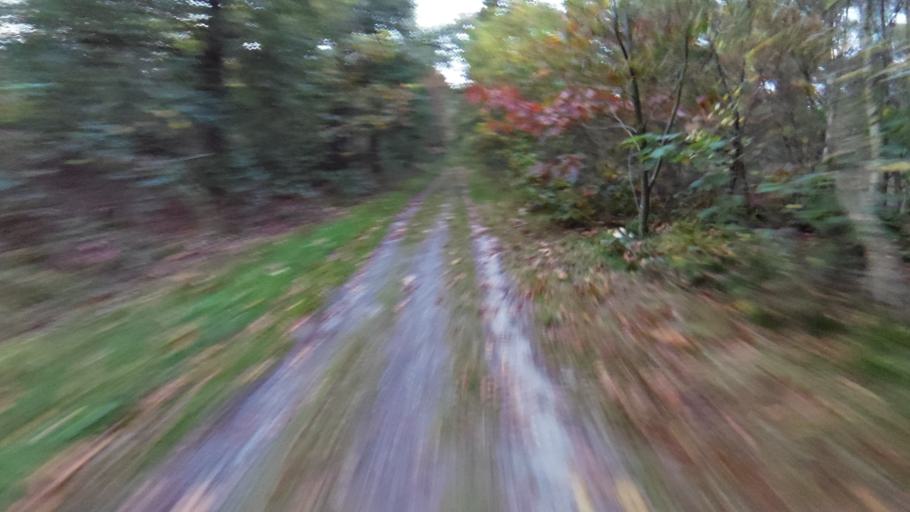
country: NL
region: Gelderland
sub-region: Gemeente Renkum
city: Oosterbeek
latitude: 52.0144
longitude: 5.8437
